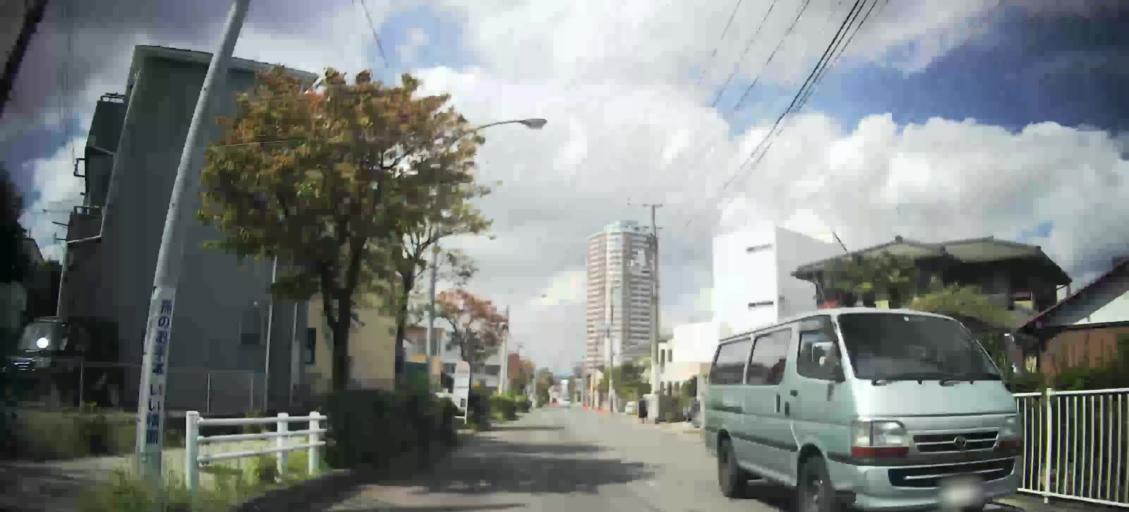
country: JP
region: Kanagawa
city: Yokohama
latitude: 35.4723
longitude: 139.5524
